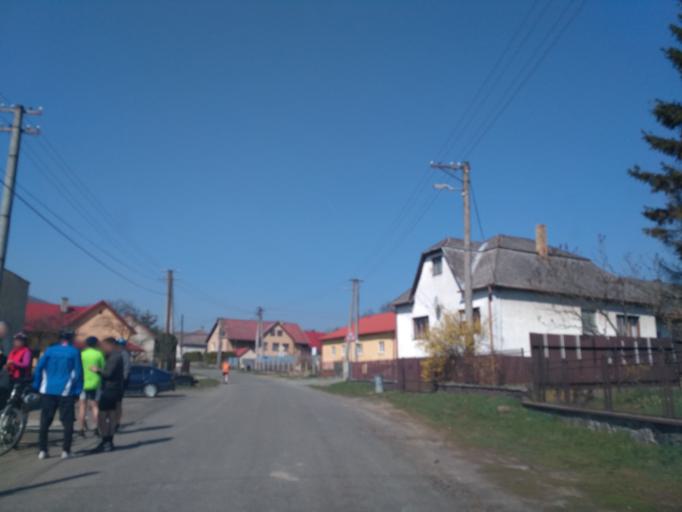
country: SK
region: Presovsky
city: Vranov nad Topl'ou
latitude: 48.8046
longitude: 21.6409
